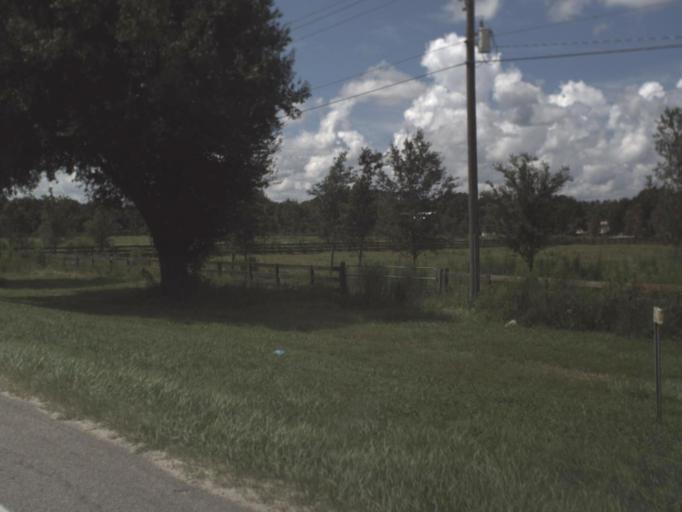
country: US
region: Florida
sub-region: Polk County
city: Polk City
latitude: 28.2221
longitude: -81.8206
